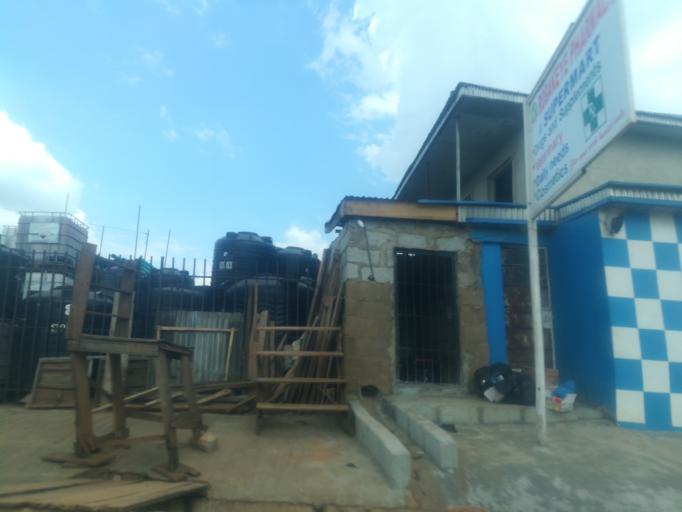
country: NG
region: Oyo
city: Ido
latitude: 7.4322
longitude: 3.8353
